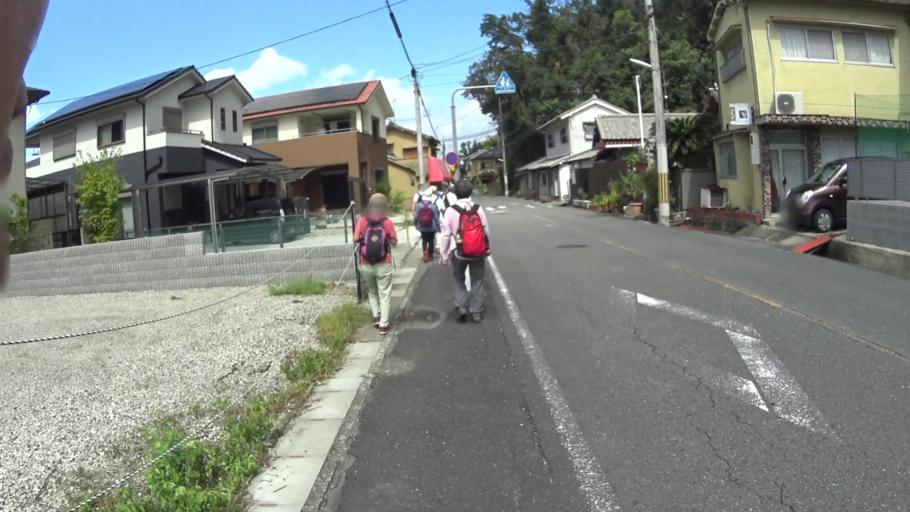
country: JP
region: Nara
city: Sakurai
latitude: 34.5046
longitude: 135.8527
